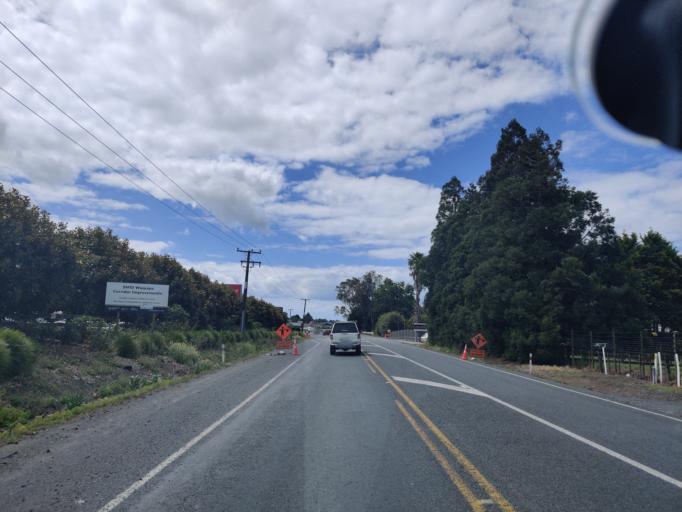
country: NZ
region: Northland
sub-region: Far North District
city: Kerikeri
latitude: -35.2110
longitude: 173.9203
